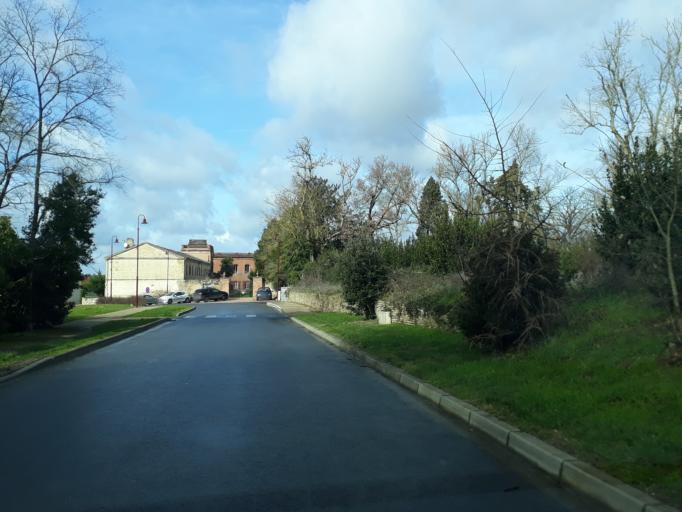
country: FR
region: Midi-Pyrenees
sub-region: Departement du Gers
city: Gimont
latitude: 43.6408
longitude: 0.9990
